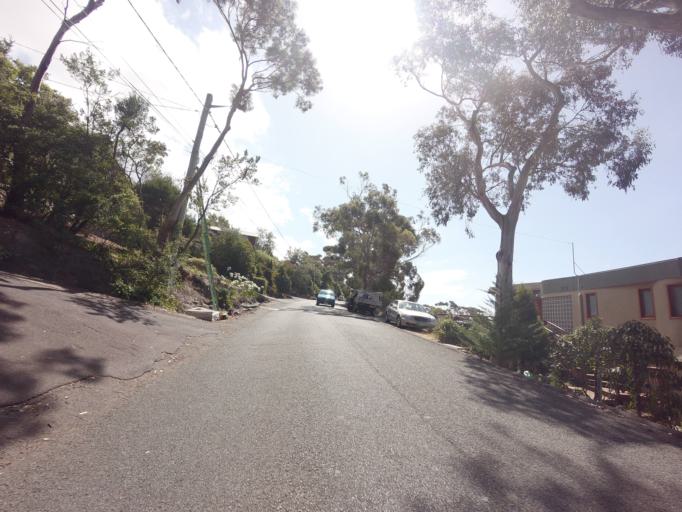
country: AU
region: Tasmania
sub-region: Hobart
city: Dynnyrne
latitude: -42.9131
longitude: 147.3274
